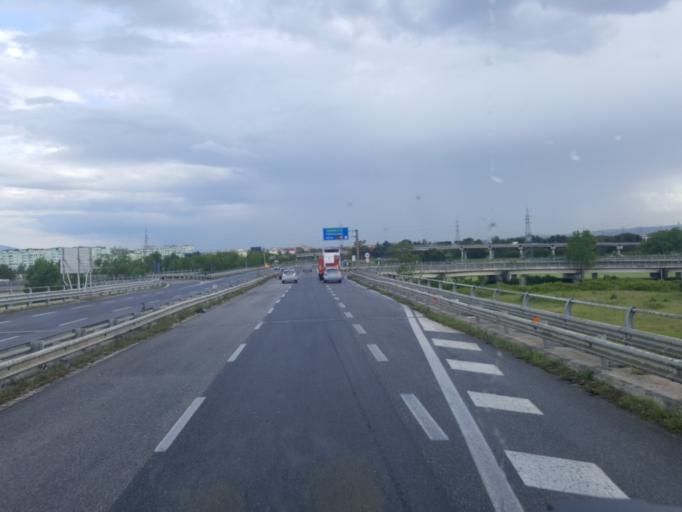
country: IT
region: Campania
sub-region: Provincia di Napoli
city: Pascarola
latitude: 40.9734
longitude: 14.2931
